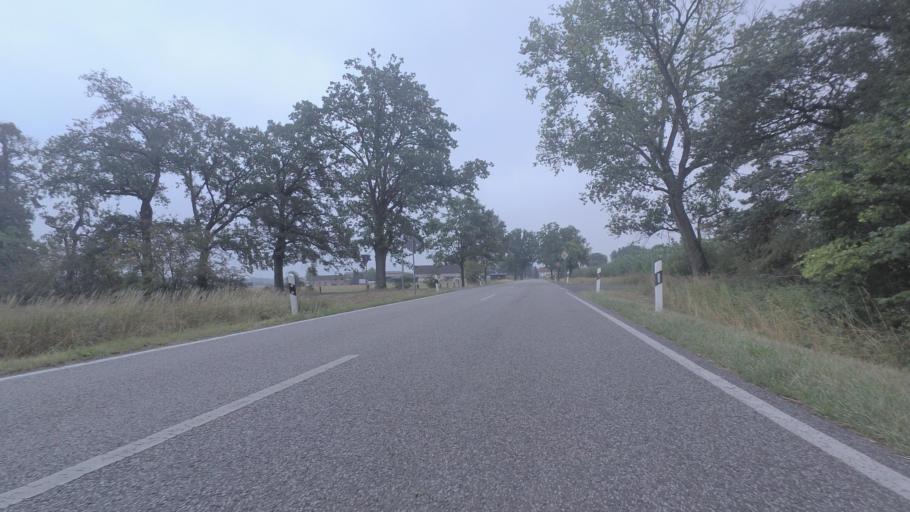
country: DE
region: Brandenburg
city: Paulinenaue
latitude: 52.6647
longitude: 12.7294
